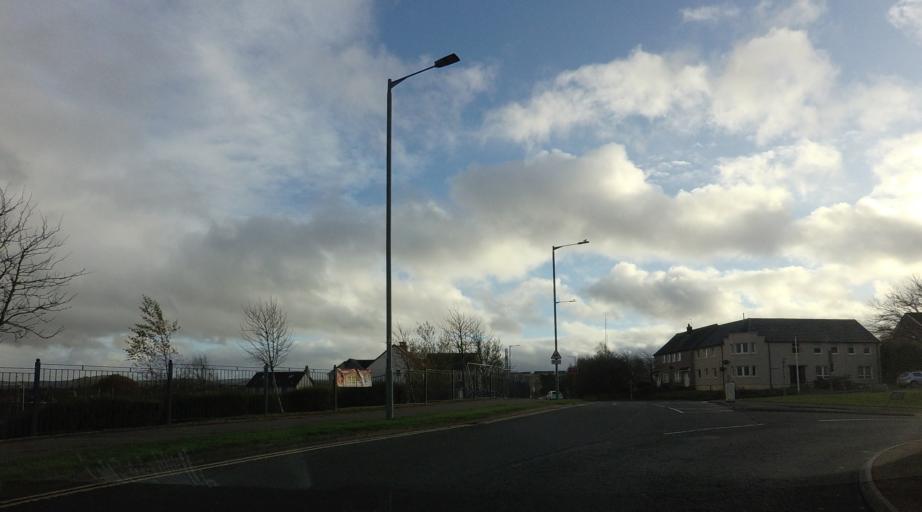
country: GB
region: Scotland
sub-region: Falkirk
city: Polmont
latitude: 55.9739
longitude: -3.7021
